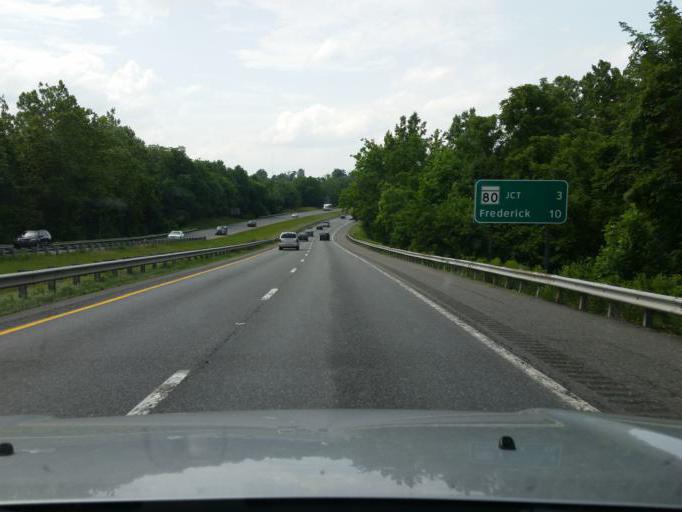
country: US
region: Maryland
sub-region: Frederick County
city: Green Valley
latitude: 39.2868
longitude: -77.3288
